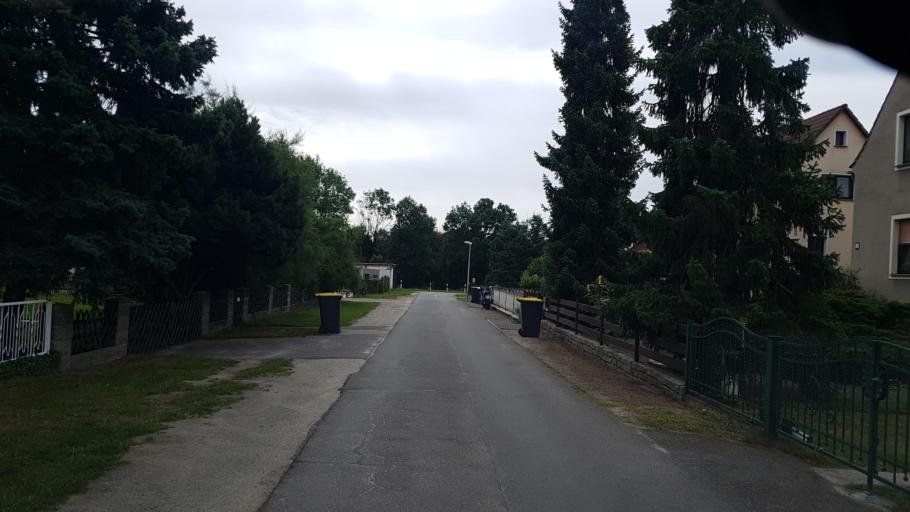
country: DE
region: Brandenburg
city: Drebkau
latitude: 51.6570
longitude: 14.2145
